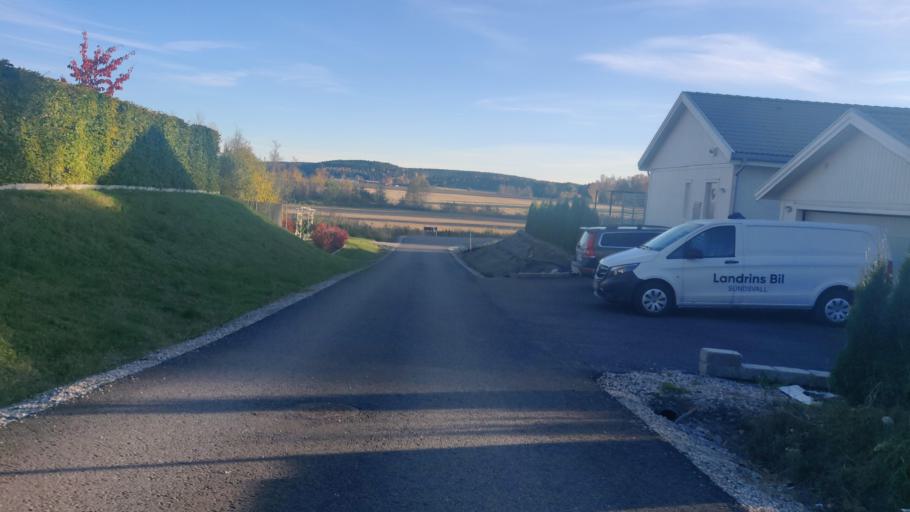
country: SE
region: Vaesternorrland
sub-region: Sundsvalls Kommun
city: Skottsund
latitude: 62.2908
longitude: 17.3945
